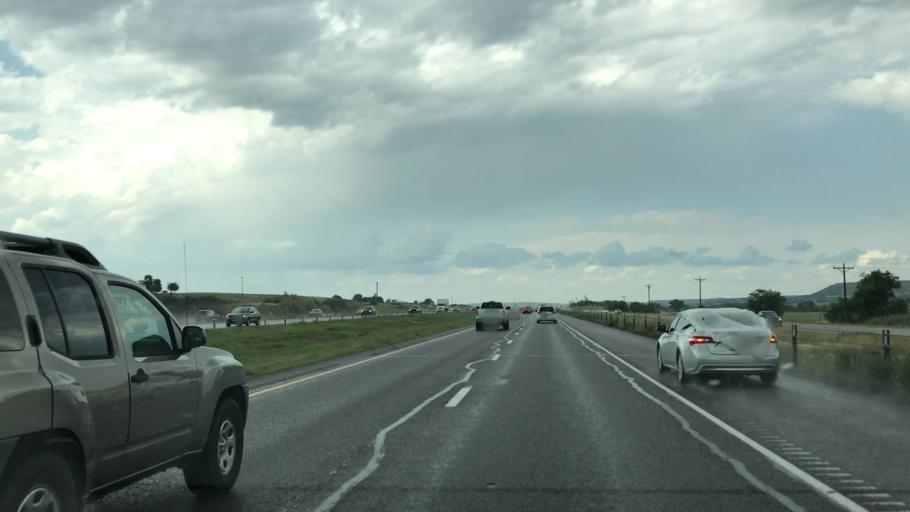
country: US
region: Colorado
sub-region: Douglas County
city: Castle Rock
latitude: 39.3021
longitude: -104.8891
